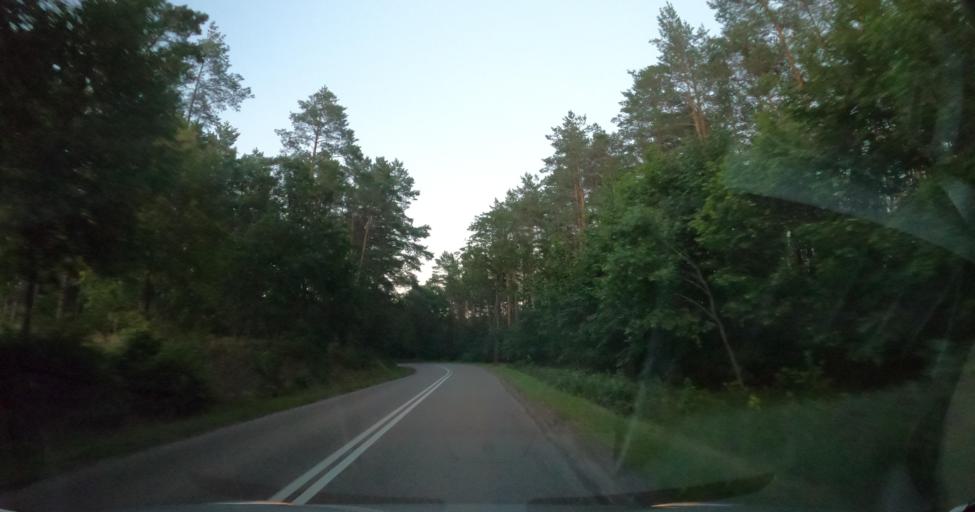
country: PL
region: Pomeranian Voivodeship
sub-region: Powiat wejherowski
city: Luzino
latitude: 54.4718
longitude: 18.0785
